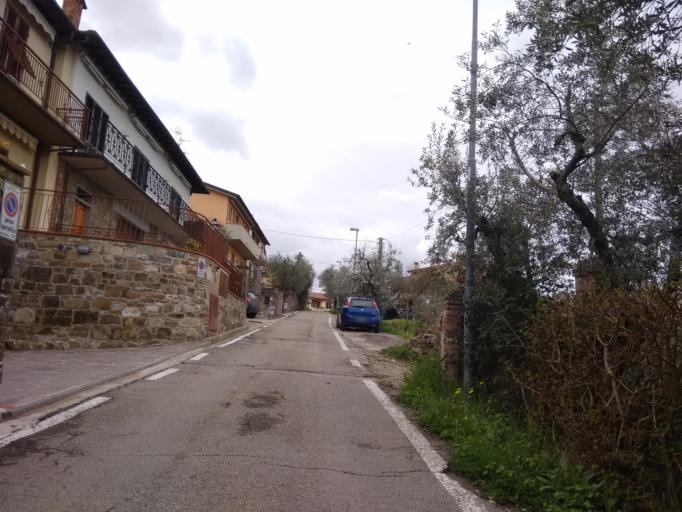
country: IT
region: Tuscany
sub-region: Province of Florence
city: Strada in Chianti
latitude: 43.6577
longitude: 11.3049
